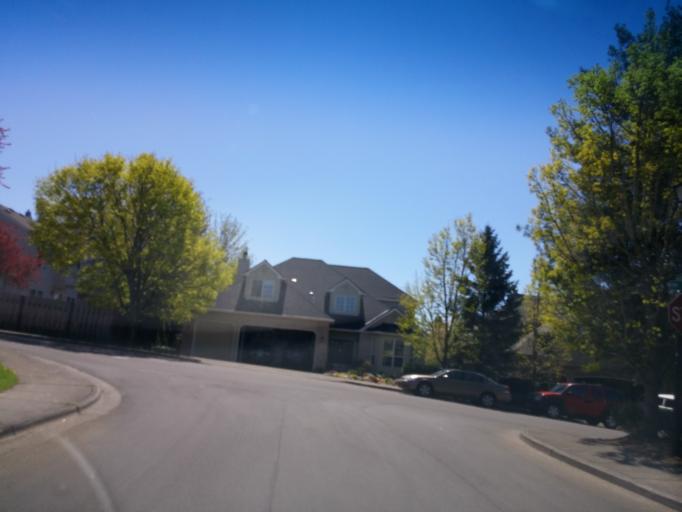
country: US
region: Oregon
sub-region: Washington County
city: West Haven
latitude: 45.5257
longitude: -122.7776
